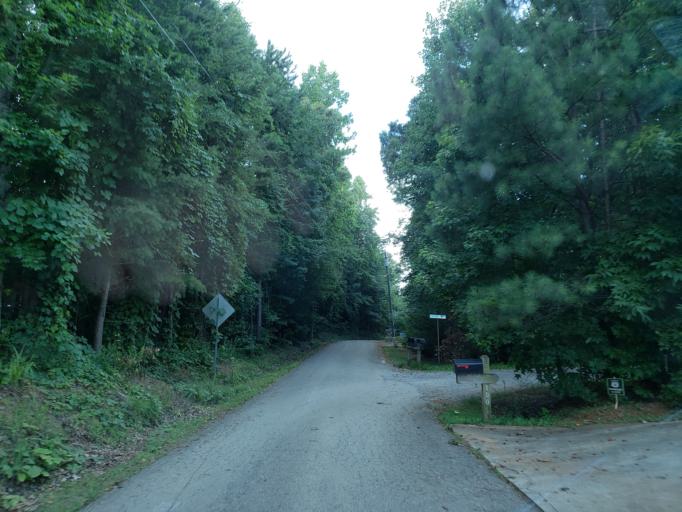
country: US
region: Georgia
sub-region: Cherokee County
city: Ball Ground
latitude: 34.3546
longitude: -84.4665
